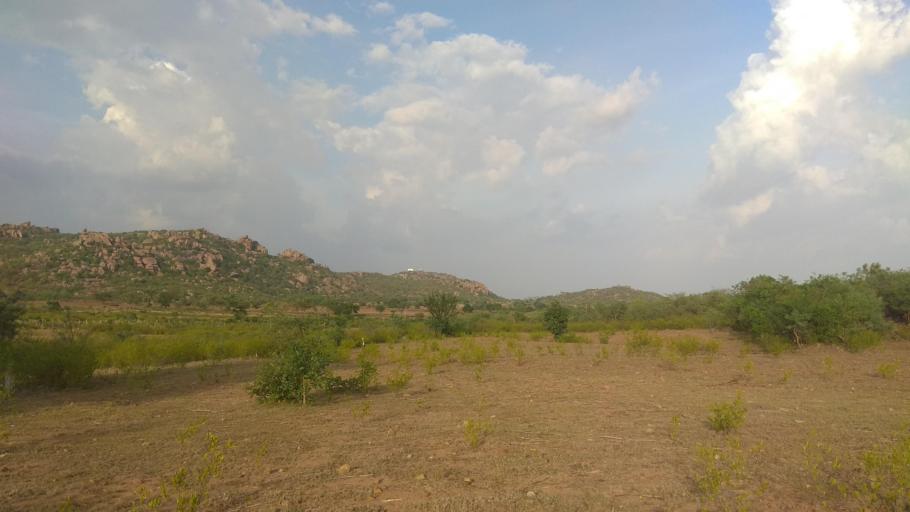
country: IN
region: Telangana
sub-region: Mahbubnagar
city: Farrukhnagar
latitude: 16.8903
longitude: 78.4833
